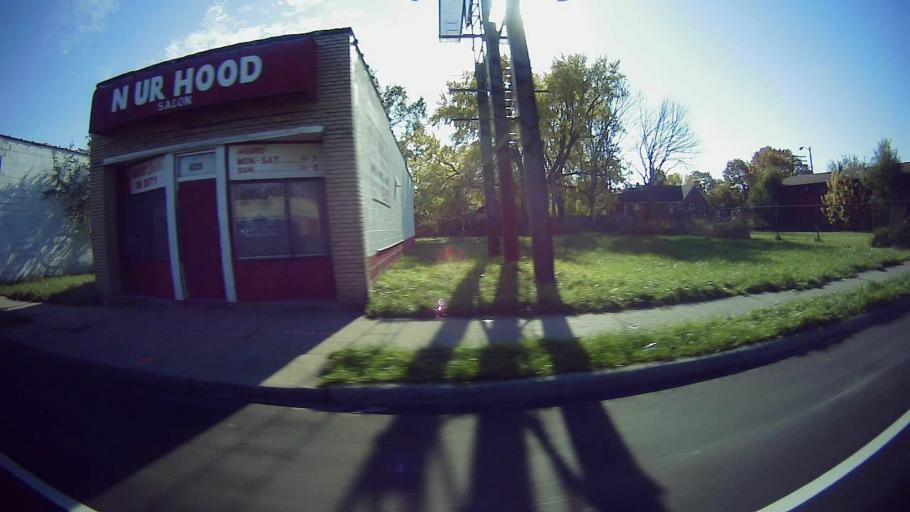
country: US
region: Michigan
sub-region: Wayne County
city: Dearborn
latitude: 42.3591
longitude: -83.1514
